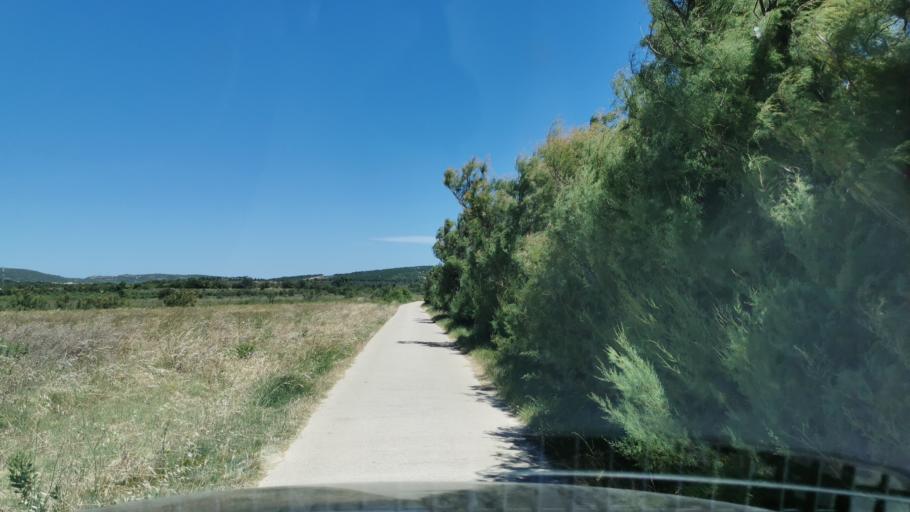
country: FR
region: Languedoc-Roussillon
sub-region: Departement de l'Aude
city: Peyriac-de-Mer
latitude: 43.0973
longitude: 2.9577
